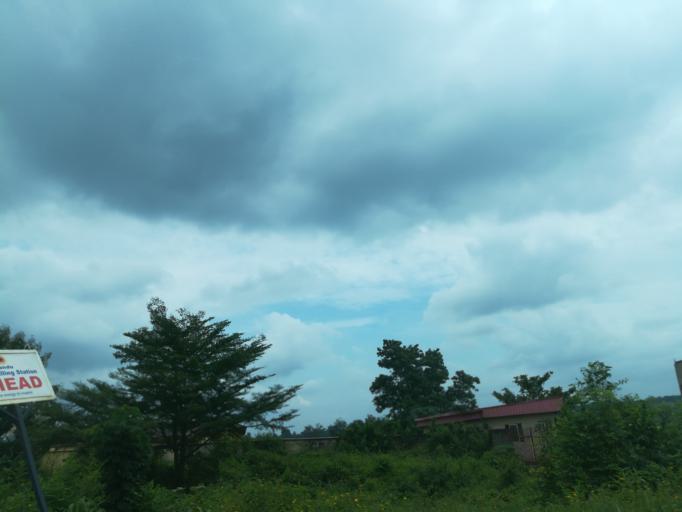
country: NG
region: Lagos
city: Ejirin
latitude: 6.6484
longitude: 3.7146
